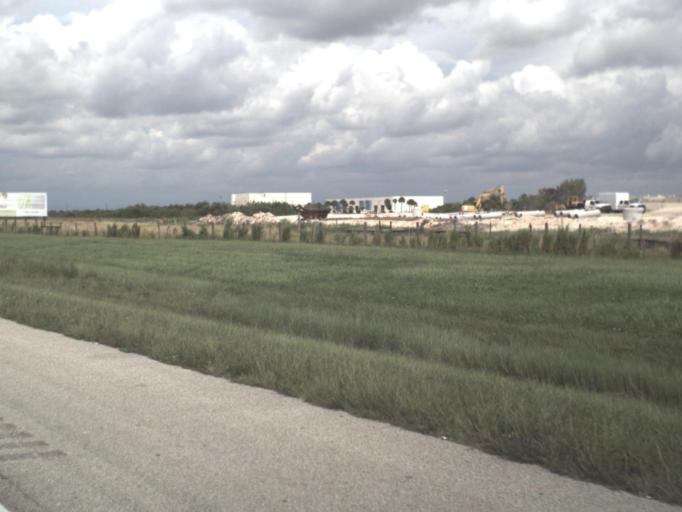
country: US
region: Florida
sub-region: Charlotte County
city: Punta Gorda
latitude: 26.9111
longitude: -82.0103
